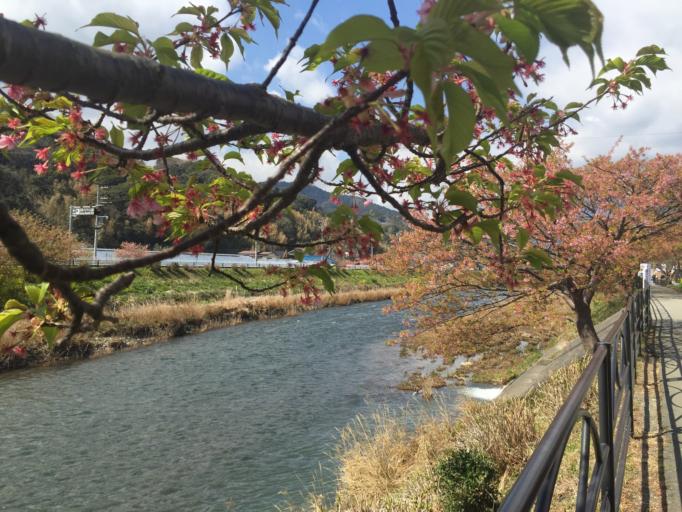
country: JP
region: Shizuoka
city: Shimoda
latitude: 34.7502
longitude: 138.9893
